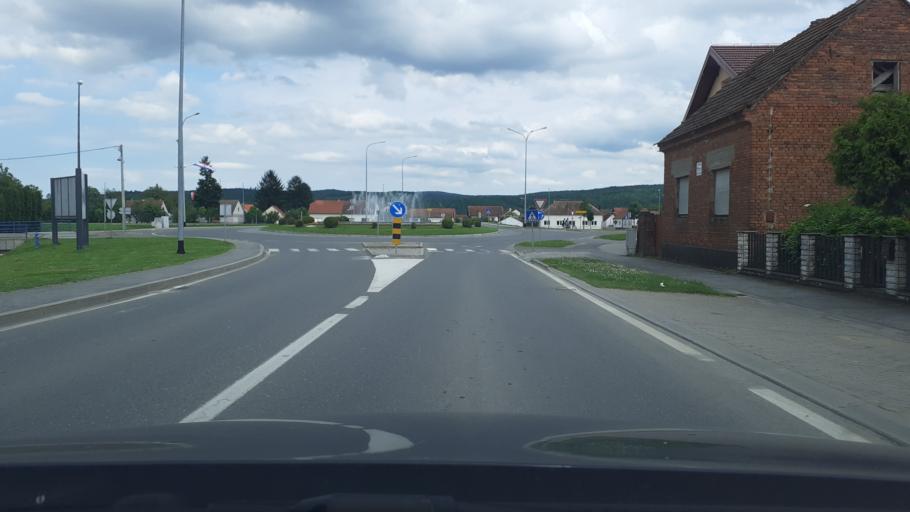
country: HR
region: Pozesko-Slavonska
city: Pleternica
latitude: 45.2837
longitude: 17.8035
